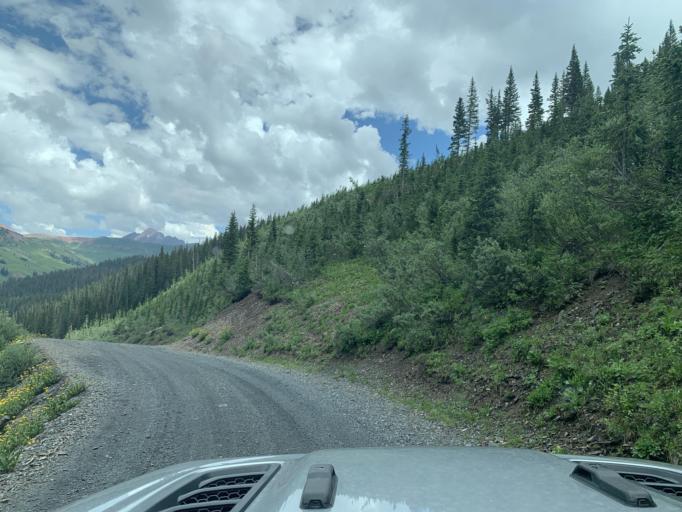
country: US
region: Colorado
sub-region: Gunnison County
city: Crested Butte
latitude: 39.0058
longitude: -107.0562
